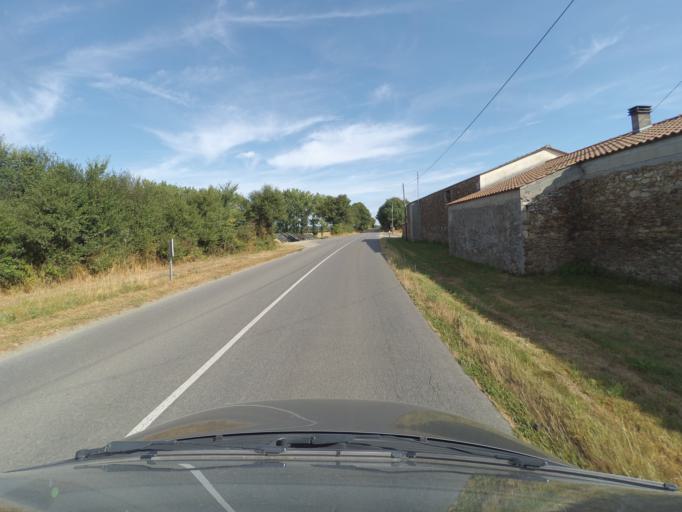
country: FR
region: Pays de la Loire
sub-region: Departement de la Loire-Atlantique
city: La Planche
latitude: 46.9965
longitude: -1.4545
